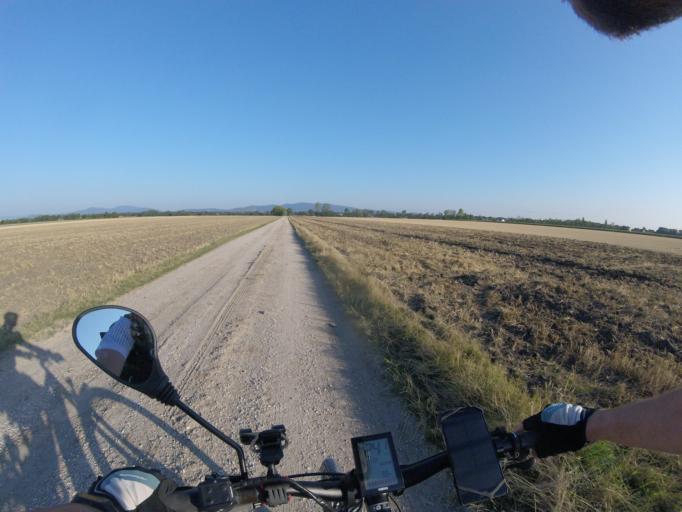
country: AT
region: Lower Austria
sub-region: Politischer Bezirk Baden
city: Trumau
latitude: 47.9845
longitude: 16.3515
